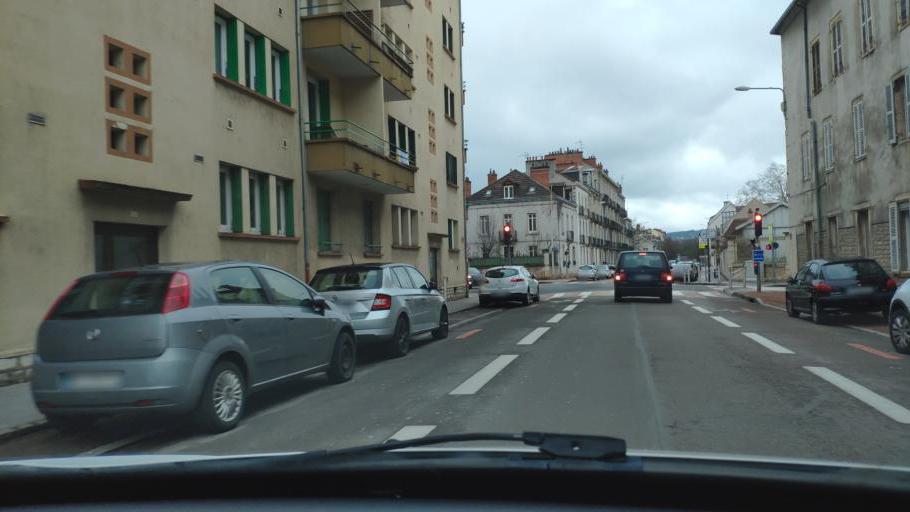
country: FR
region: Bourgogne
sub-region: Departement de la Cote-d'Or
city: Dijon
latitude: 47.3169
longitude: 5.0402
